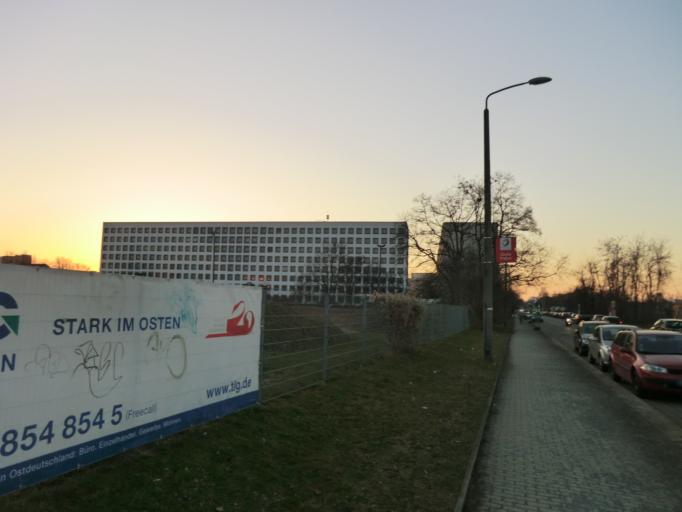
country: DE
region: Saxony
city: Dresden
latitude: 51.0357
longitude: 13.7431
